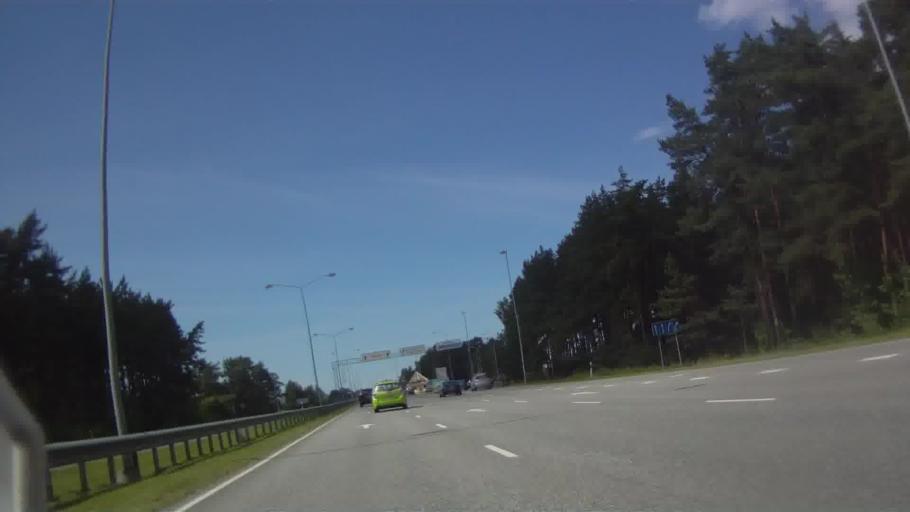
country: LV
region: Babite
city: Pinki
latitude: 56.9682
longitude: 23.8693
